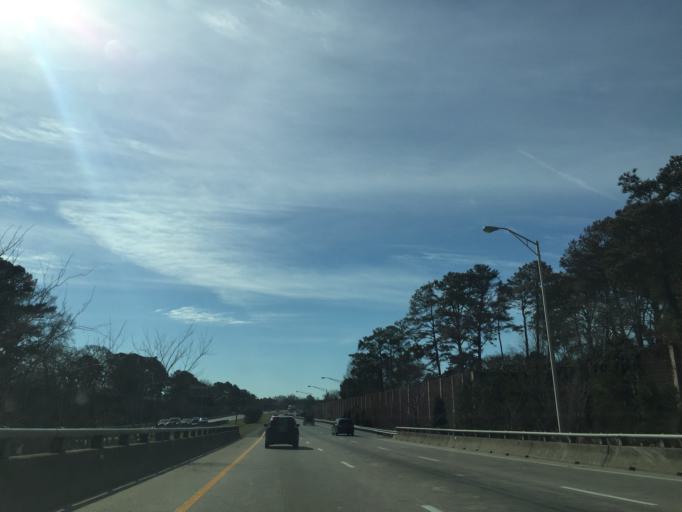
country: US
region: Virginia
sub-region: City of Norfolk
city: Norfolk
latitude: 36.9415
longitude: -76.2661
